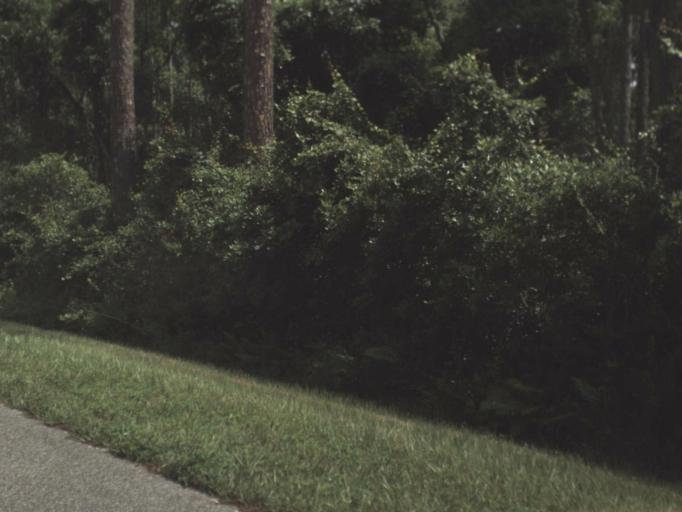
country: US
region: Florida
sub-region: Putnam County
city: East Palatka
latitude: 29.5936
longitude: -81.5694
